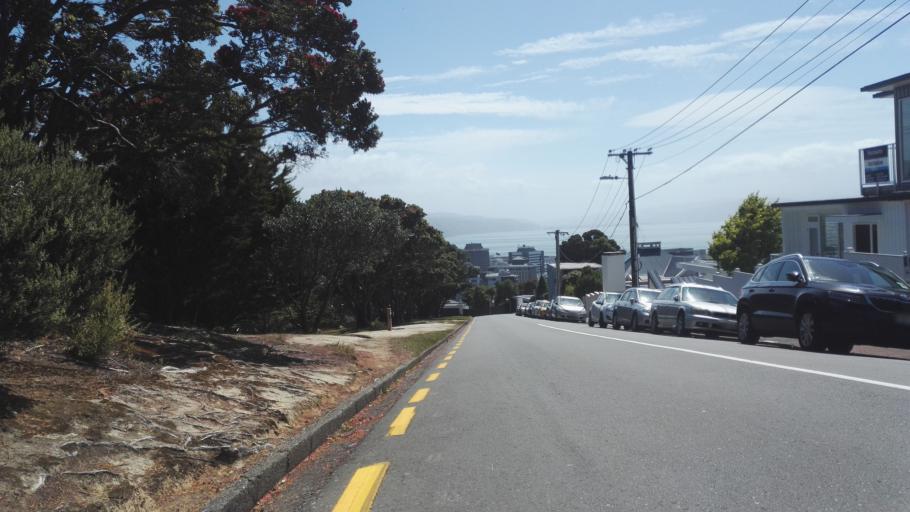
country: NZ
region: Wellington
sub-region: Wellington City
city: Kelburn
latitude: -41.2829
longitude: 174.7699
